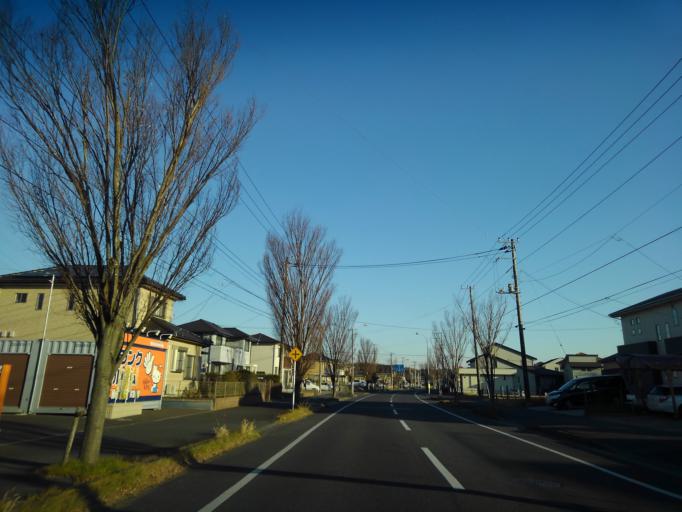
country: JP
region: Chiba
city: Kimitsu
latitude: 35.3112
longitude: 139.9198
